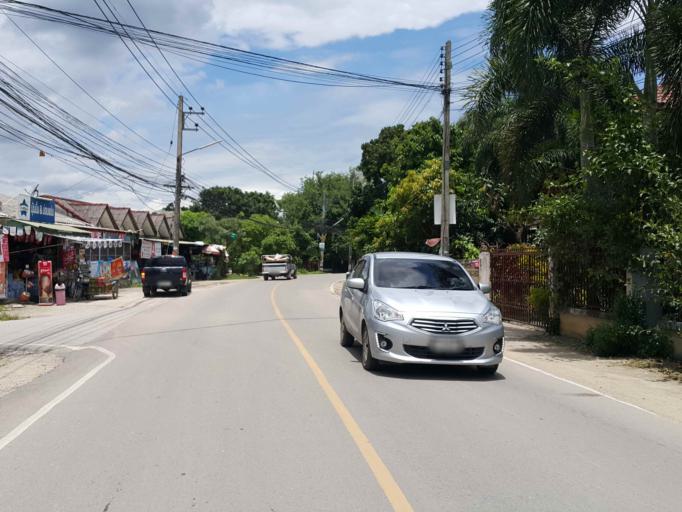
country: TH
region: Chiang Mai
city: San Sai
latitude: 18.8617
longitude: 98.9835
